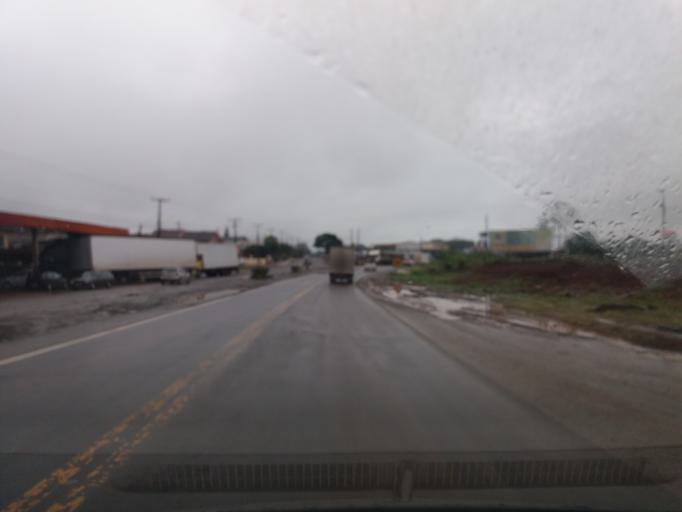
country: BR
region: Parana
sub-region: Realeza
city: Realeza
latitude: -25.4966
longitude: -53.5997
